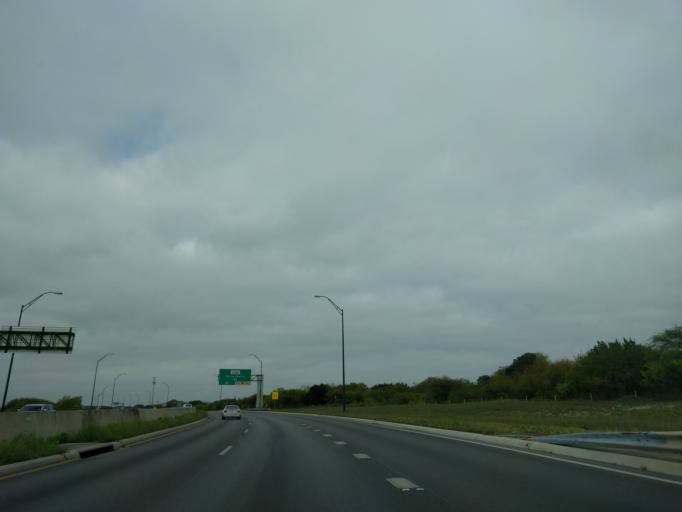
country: US
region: Texas
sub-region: Bexar County
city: Windcrest
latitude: 29.5356
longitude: -98.4056
